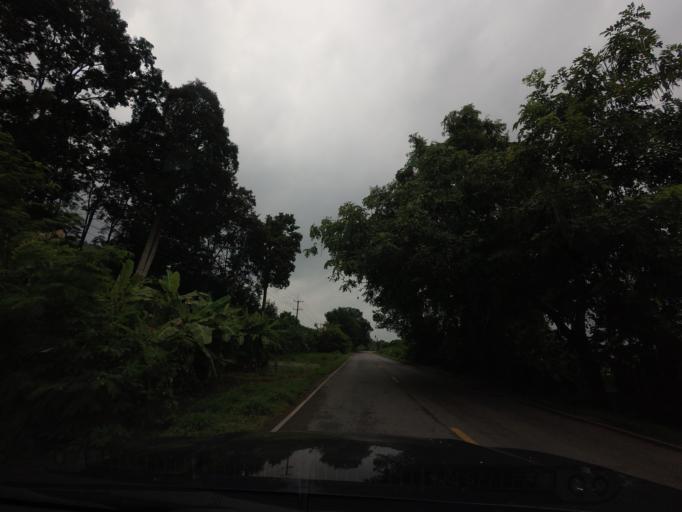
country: TH
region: Nong Khai
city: Sangkhom
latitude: 18.0448
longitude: 102.3342
